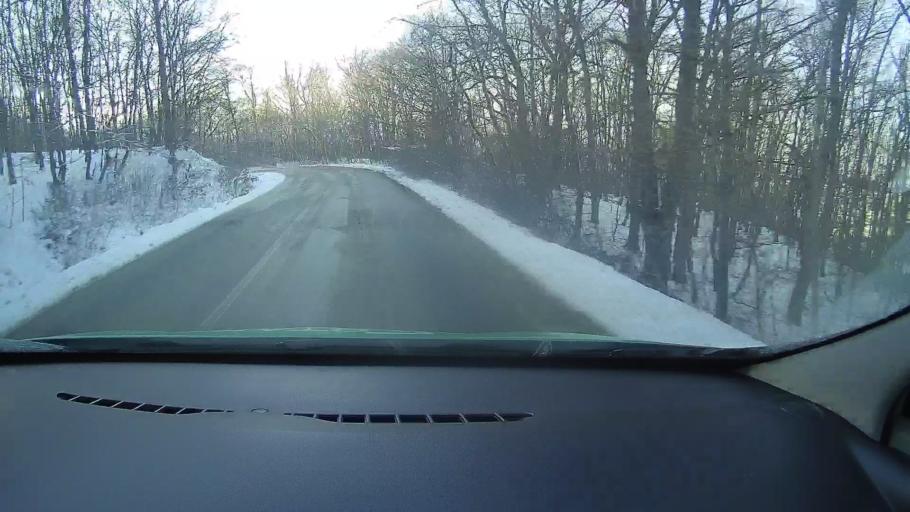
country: RO
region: Sibiu
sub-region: Oras Agnita
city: Ruja
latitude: 45.9872
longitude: 24.6759
